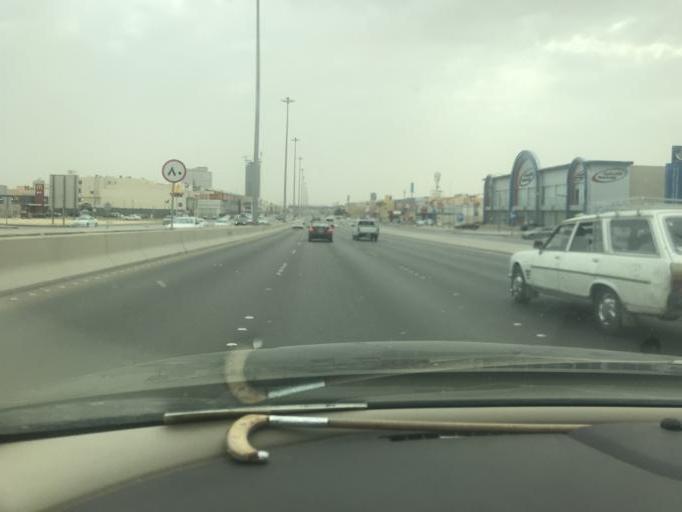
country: SA
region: Ar Riyad
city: Riyadh
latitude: 24.8171
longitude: 46.6385
